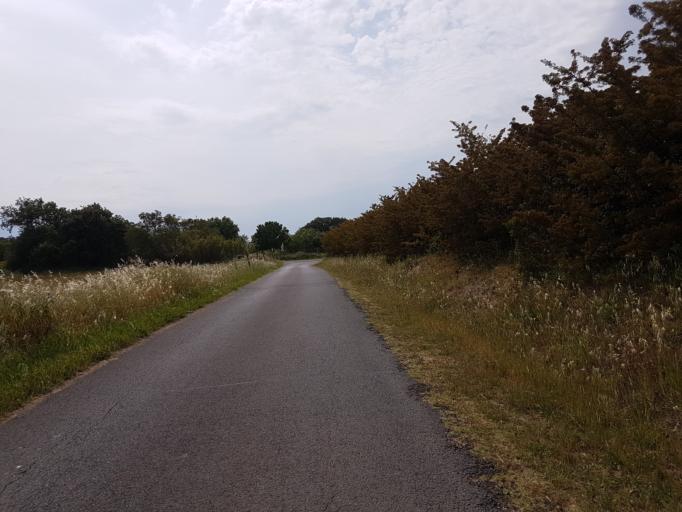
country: FR
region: Languedoc-Roussillon
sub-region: Departement de l'Herault
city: Portiragnes
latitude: 43.3106
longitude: 3.3588
